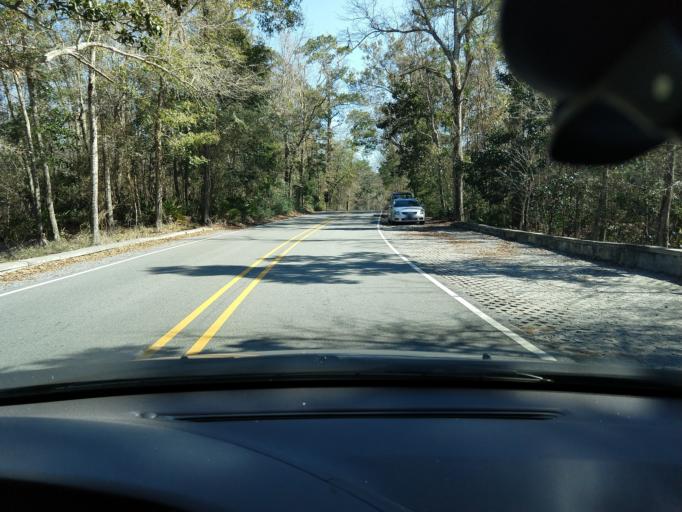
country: US
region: Mississippi
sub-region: Jackson County
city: Gulf Park Estates
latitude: 30.3979
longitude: -88.7899
